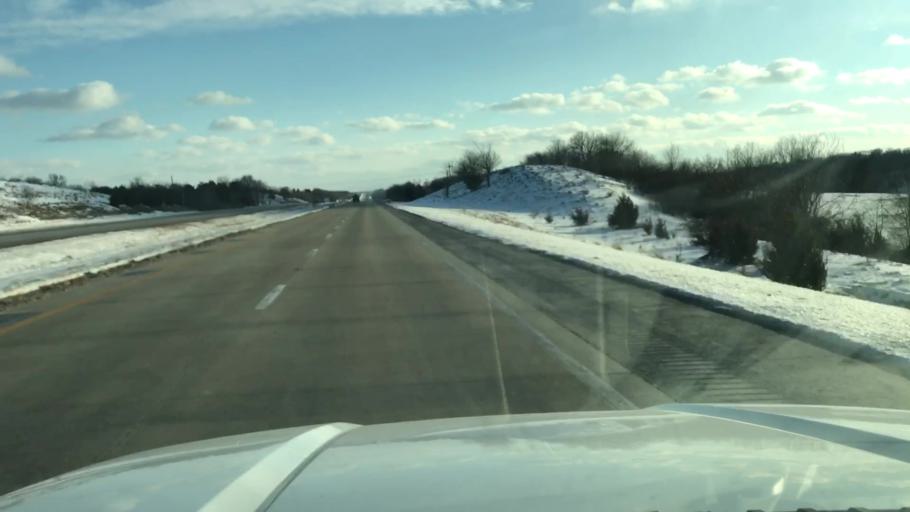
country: US
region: Missouri
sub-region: Andrew County
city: Savannah
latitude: 39.9511
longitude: -94.8603
